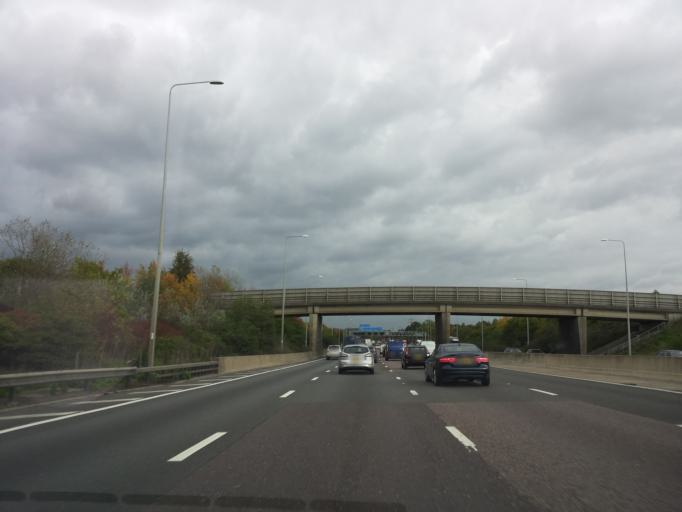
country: GB
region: England
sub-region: Hertfordshire
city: Radlett
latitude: 51.7115
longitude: -0.3127
